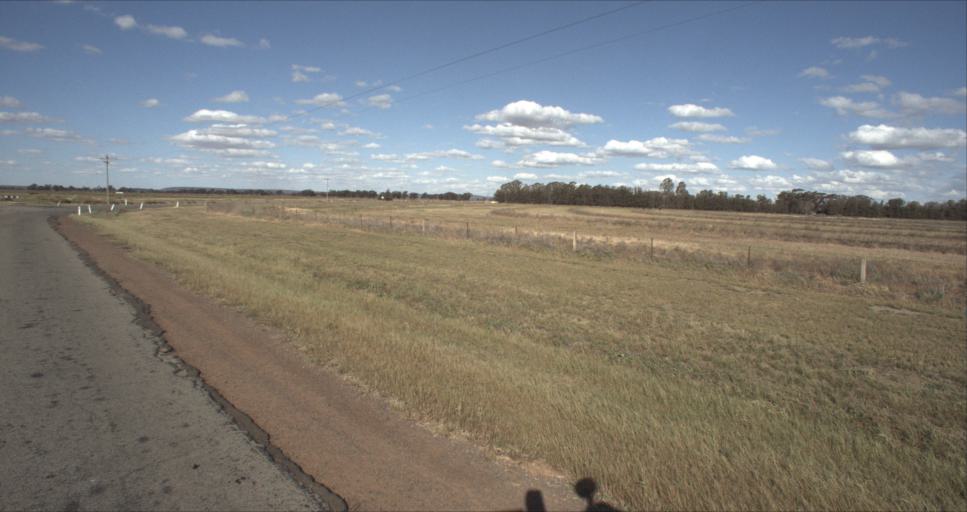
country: AU
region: New South Wales
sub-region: Leeton
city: Leeton
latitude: -34.4555
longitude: 146.2742
